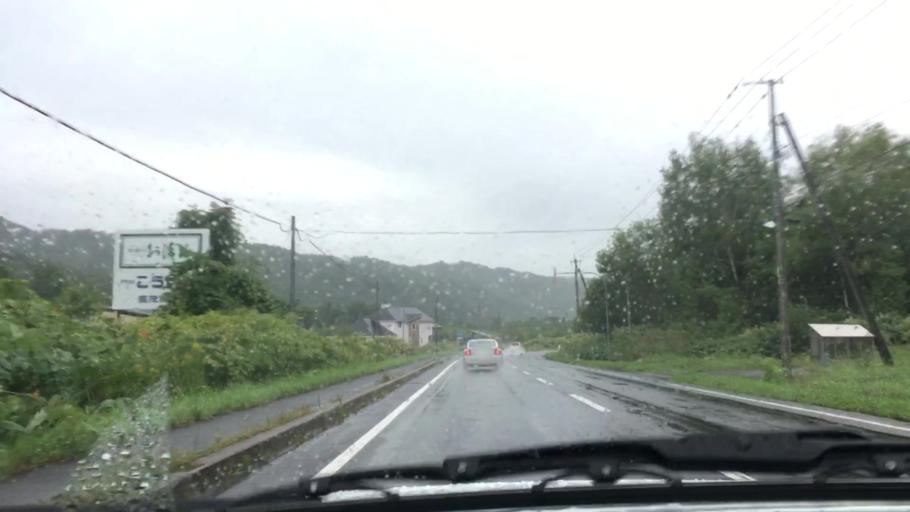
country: JP
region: Hokkaido
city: Niseko Town
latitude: 42.8098
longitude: 141.0014
